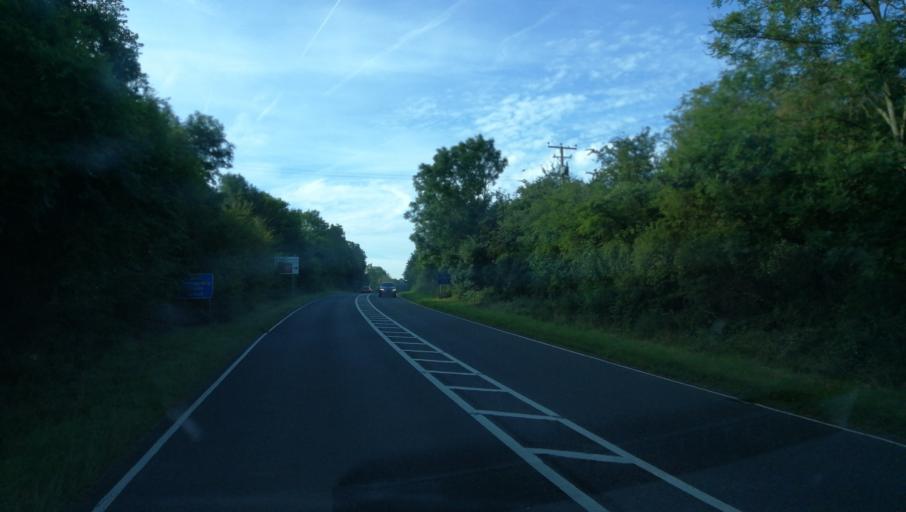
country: GB
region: England
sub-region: Oxfordshire
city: Deddington
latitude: 51.9569
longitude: -1.3181
